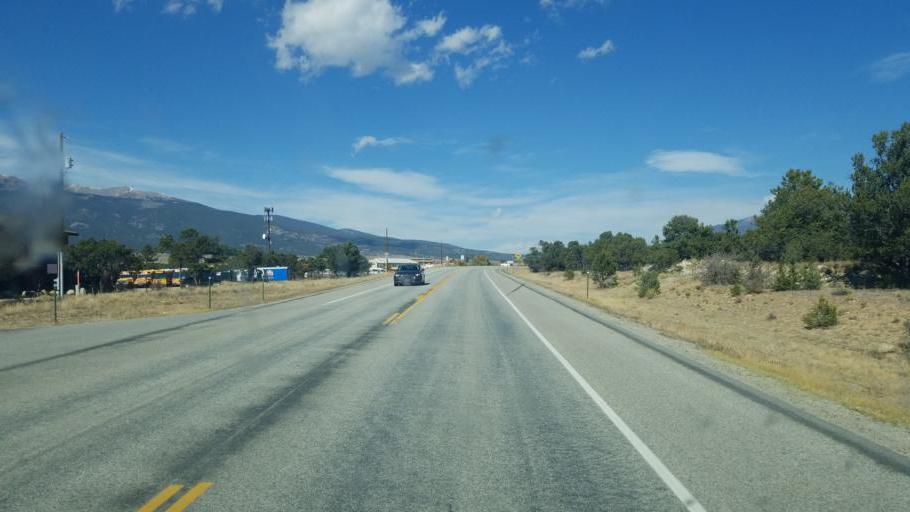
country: US
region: Colorado
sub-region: Chaffee County
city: Buena Vista
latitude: 38.8726
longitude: -106.1575
